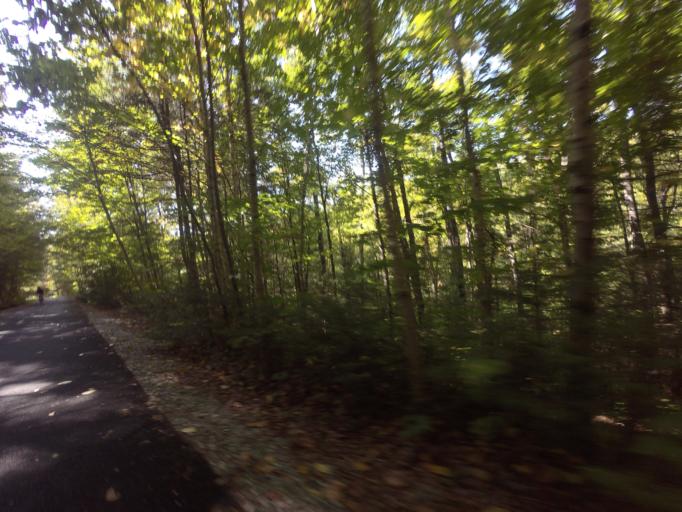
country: CA
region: Quebec
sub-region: Laurentides
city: Mont-Tremblant
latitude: 46.1255
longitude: -74.4977
